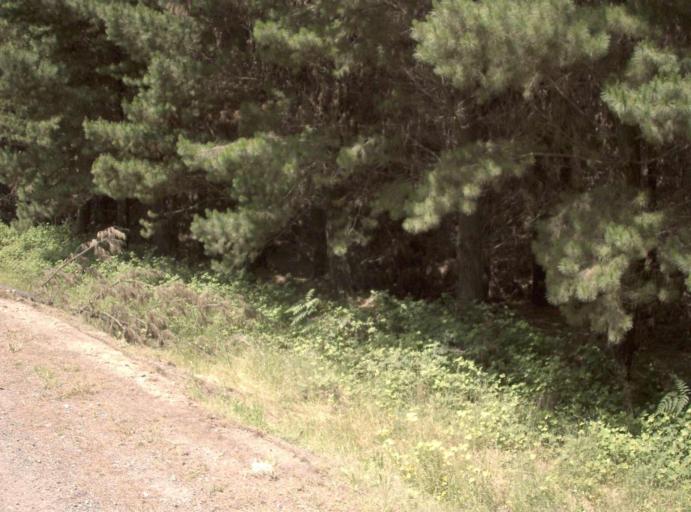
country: AU
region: Victoria
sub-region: Latrobe
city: Traralgon
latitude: -38.3826
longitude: 146.6657
